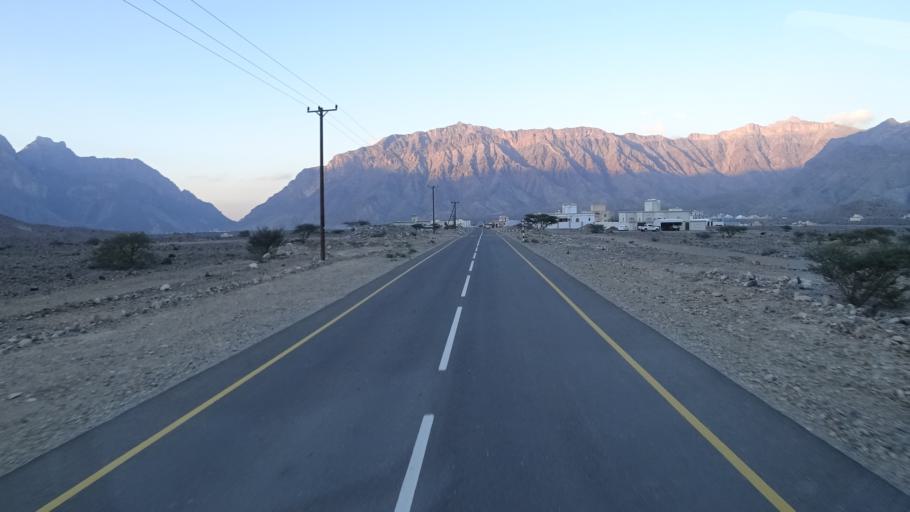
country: OM
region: Al Batinah
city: Rustaq
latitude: 23.2727
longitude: 57.3256
